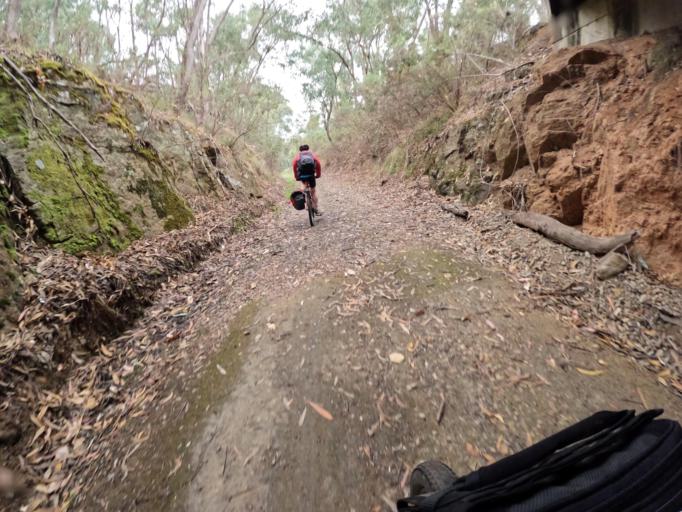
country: AU
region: New South Wales
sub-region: Greater Hume Shire
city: Holbrook
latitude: -36.1673
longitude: 147.4055
